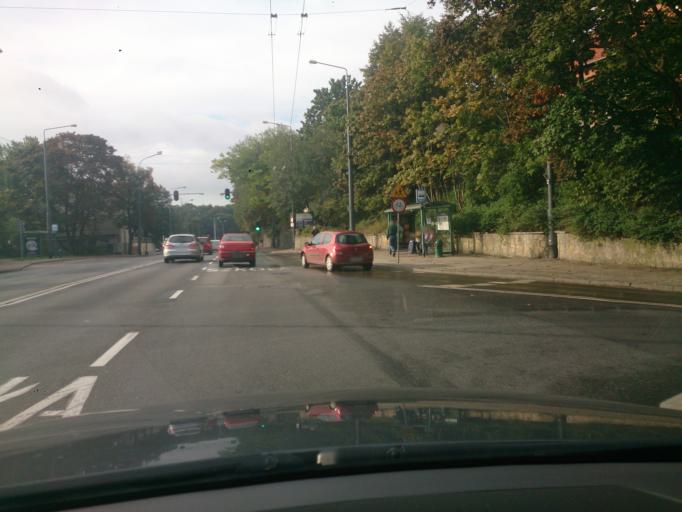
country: PL
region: Pomeranian Voivodeship
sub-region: Sopot
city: Sopot
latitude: 54.4534
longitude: 18.5554
